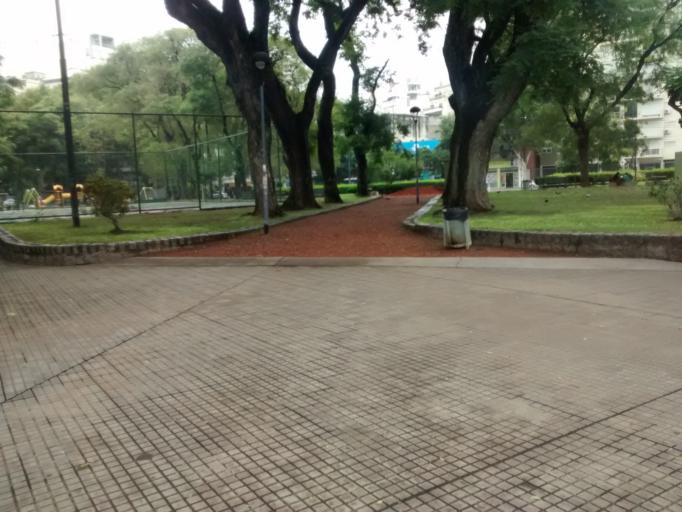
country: AR
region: Buenos Aires F.D.
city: Colegiales
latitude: -34.6062
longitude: -58.4482
